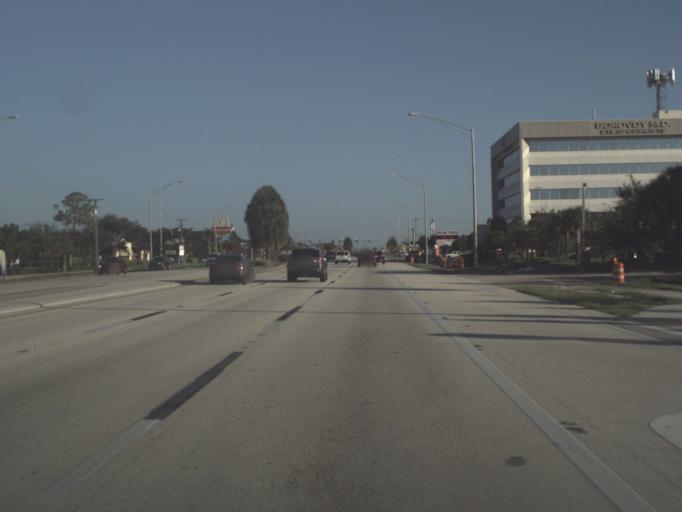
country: US
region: Florida
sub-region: Lee County
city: Villas
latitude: 26.5611
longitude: -81.8718
